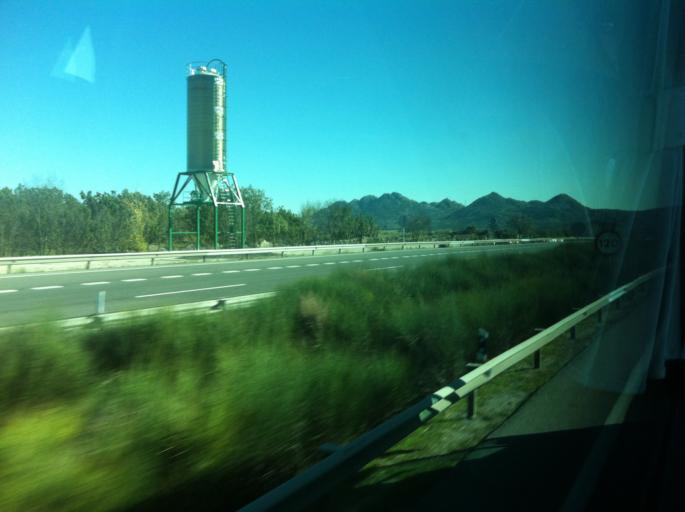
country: ES
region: Madrid
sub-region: Provincia de Madrid
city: La Cabrera
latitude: 40.9154
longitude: -3.6097
